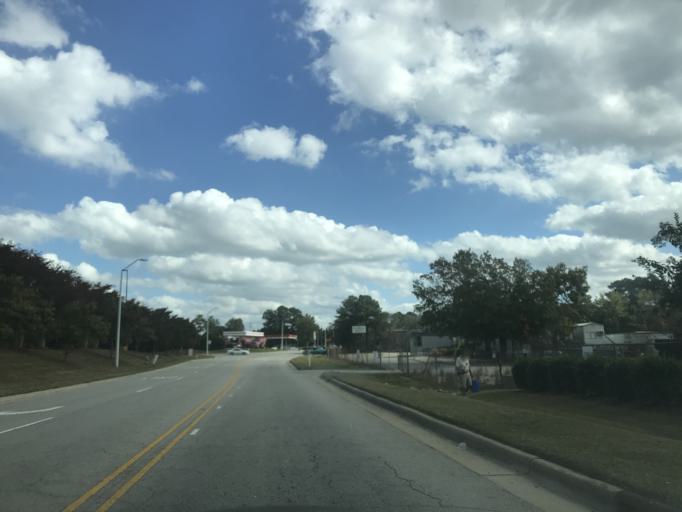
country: US
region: North Carolina
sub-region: Wake County
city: Garner
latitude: 35.7176
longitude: -78.6582
